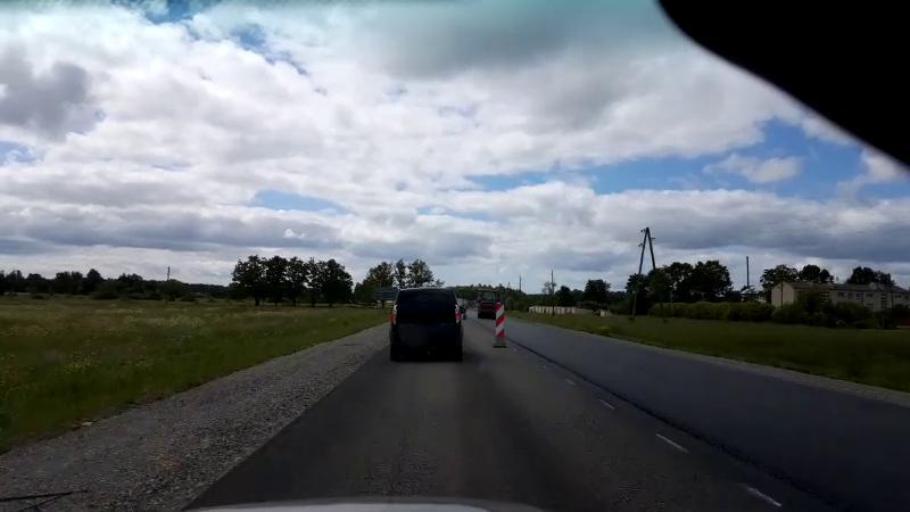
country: LV
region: Salacgrivas
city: Ainazi
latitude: 57.8581
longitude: 24.3661
